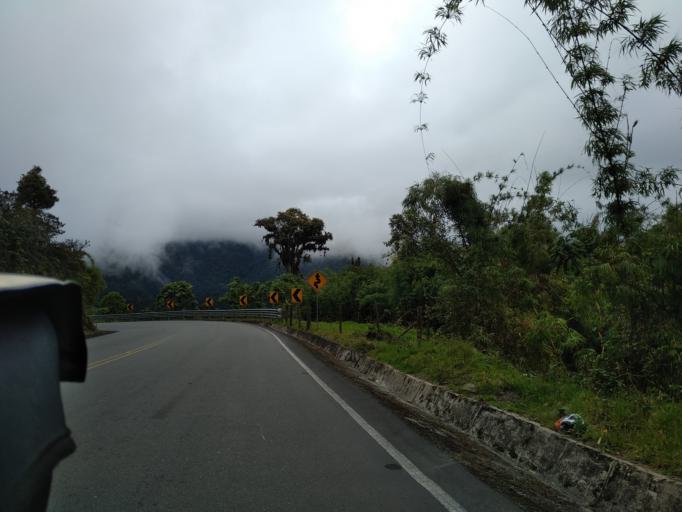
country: EC
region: Cotopaxi
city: La Mana
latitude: -0.9654
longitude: -78.9883
